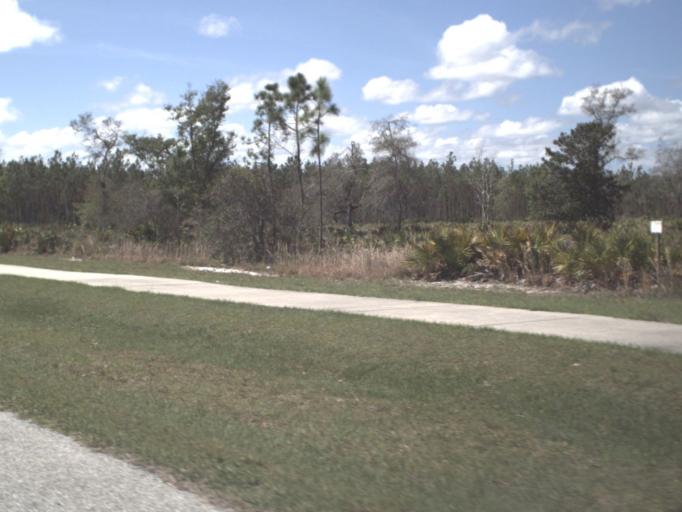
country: US
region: Florida
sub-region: Flagler County
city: Palm Coast
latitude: 29.6239
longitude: -81.2826
